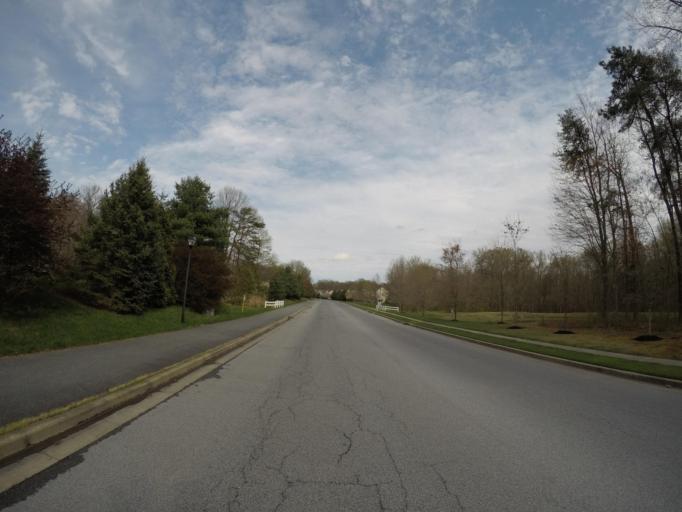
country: US
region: Delaware
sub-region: New Castle County
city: Glasgow
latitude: 39.5610
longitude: -75.7569
